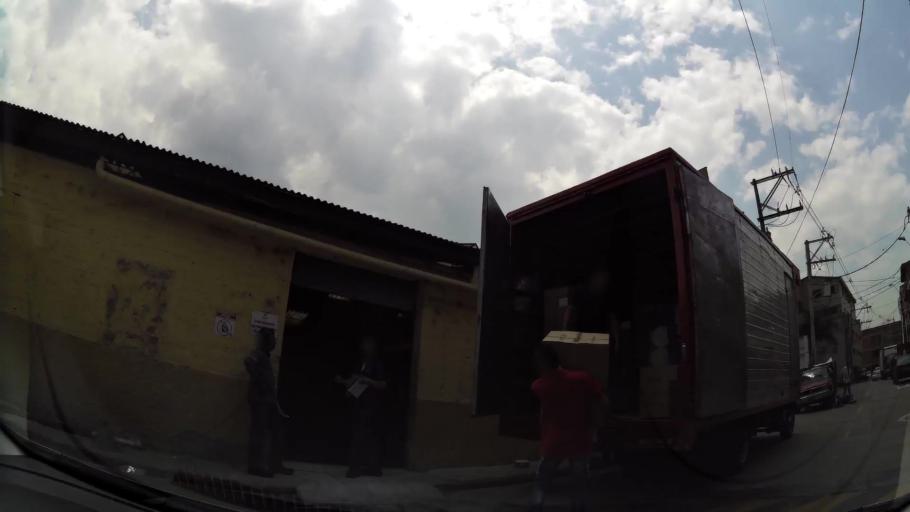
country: CO
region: Antioquia
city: Itagui
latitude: 6.1904
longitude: -75.5965
